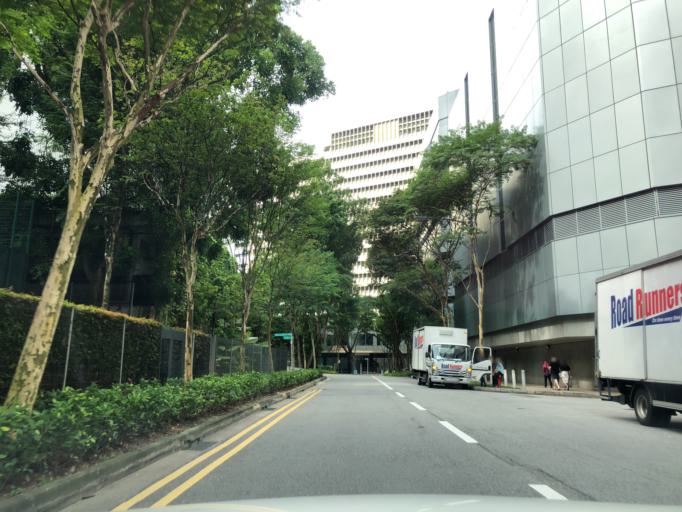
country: SG
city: Singapore
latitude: 1.2986
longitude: 103.8377
